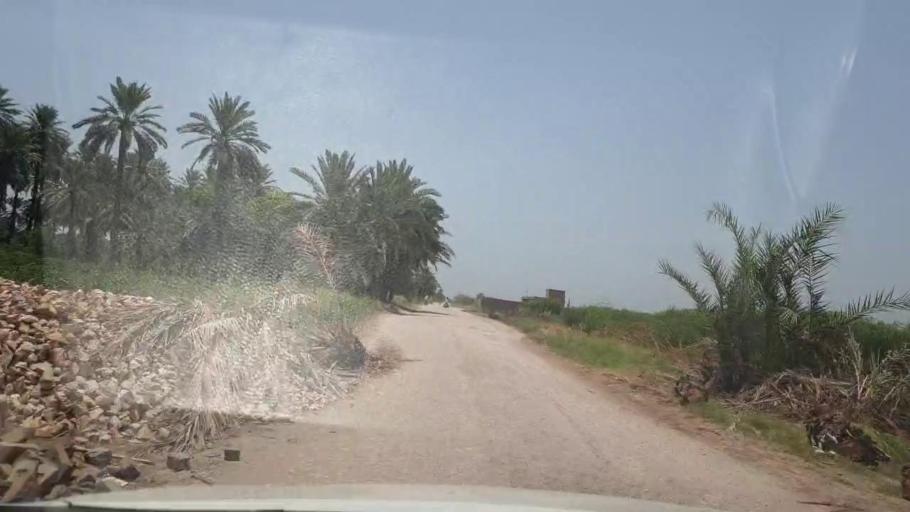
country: PK
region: Sindh
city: Bozdar
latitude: 27.1854
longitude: 68.6327
